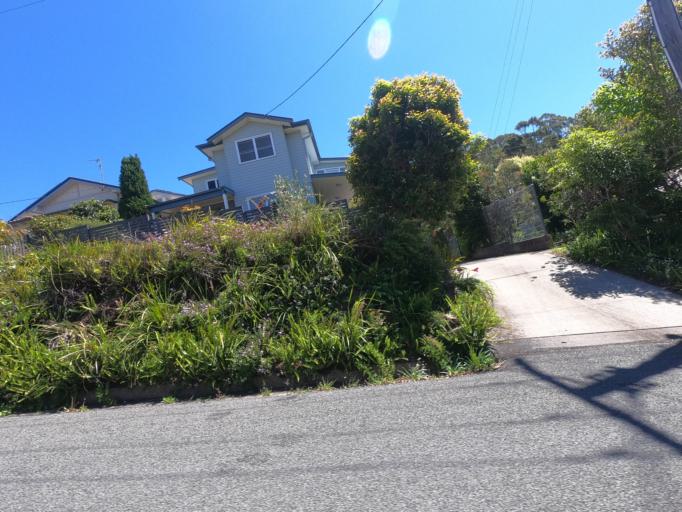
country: AU
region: New South Wales
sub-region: Wollongong
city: Bulli
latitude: -34.3026
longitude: 150.9351
